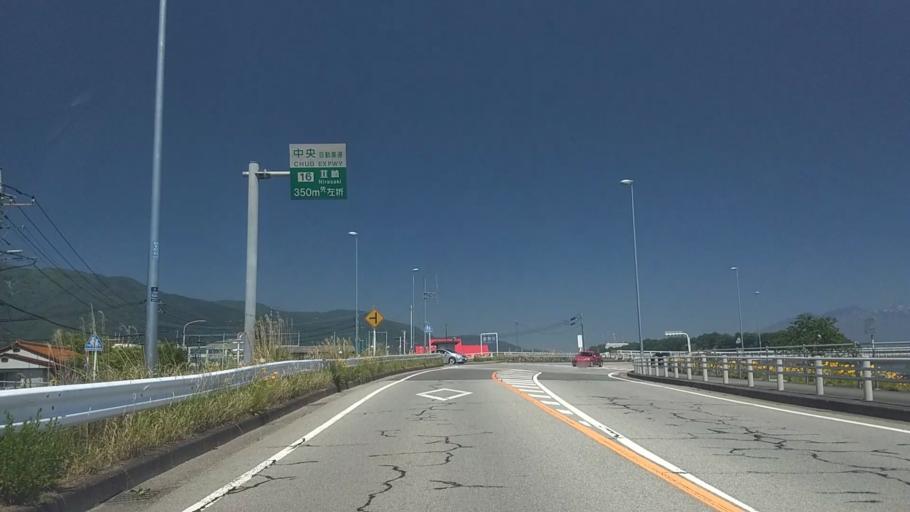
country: JP
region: Yamanashi
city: Nirasaki
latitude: 35.6985
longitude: 138.4540
